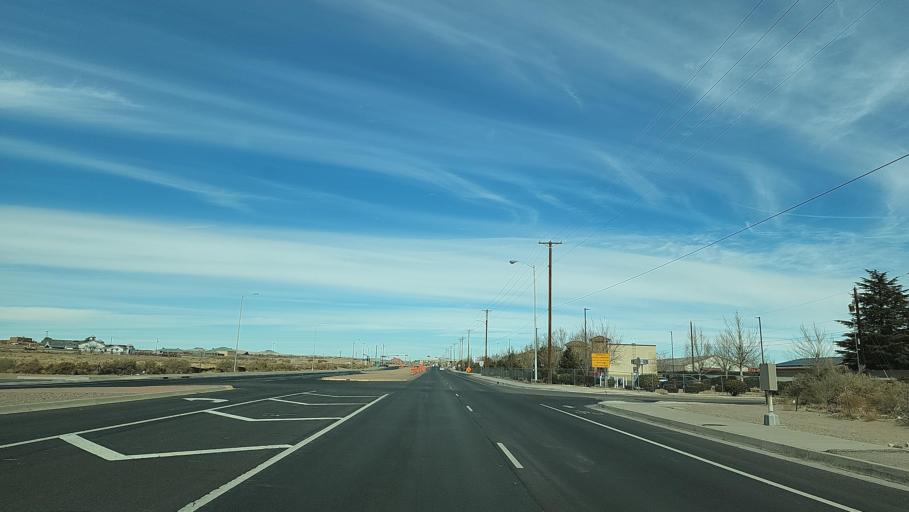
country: US
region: New Mexico
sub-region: Bernalillo County
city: South Valley
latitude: 35.0629
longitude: -106.7088
